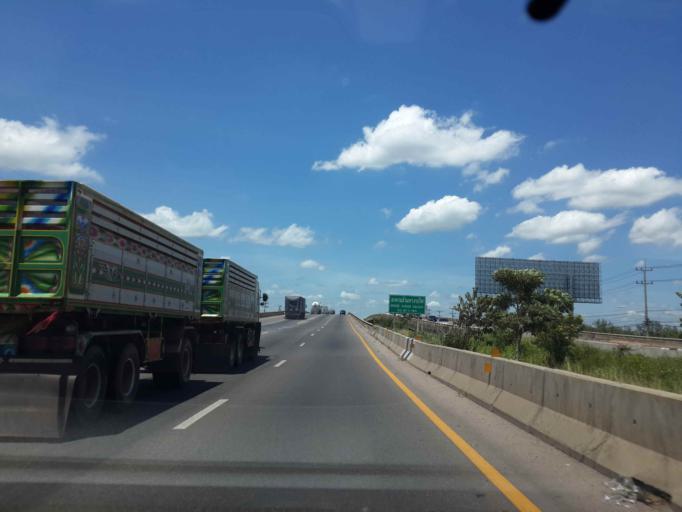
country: TH
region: Samut Sakhon
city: Ban Phaeo
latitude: 13.4831
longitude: 100.1199
